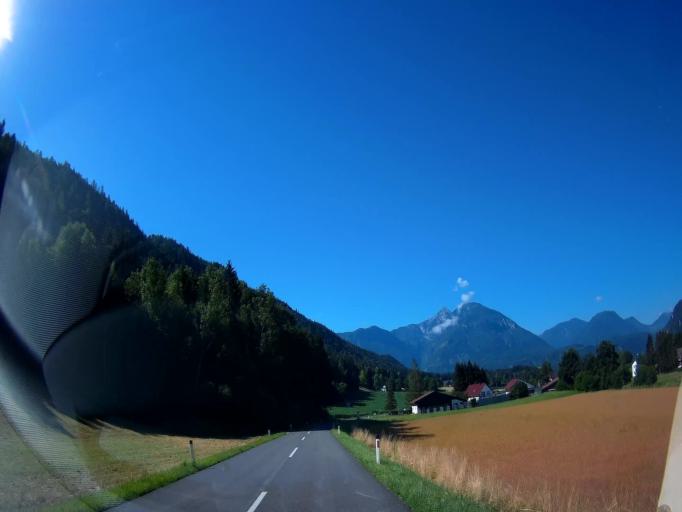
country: AT
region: Carinthia
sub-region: Politischer Bezirk Volkermarkt
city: Gallizien
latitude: 46.5966
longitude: 14.5295
